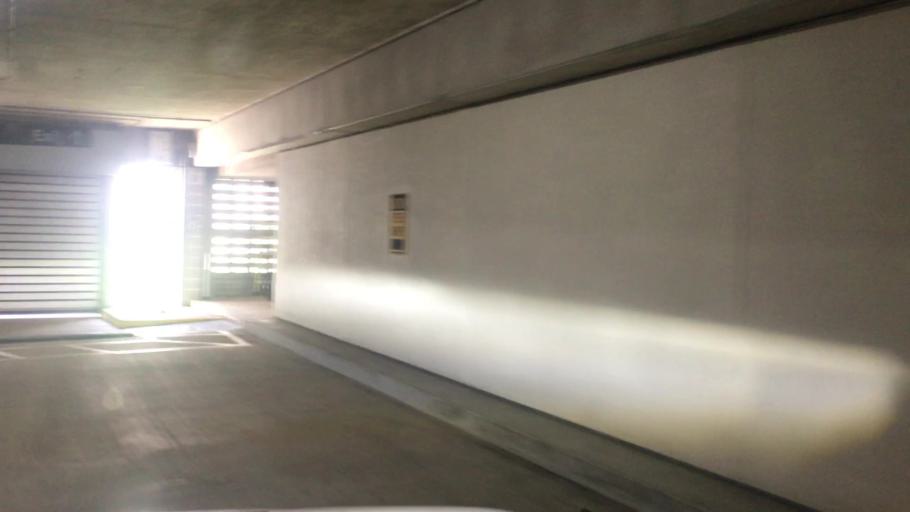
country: US
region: Texas
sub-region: Harris County
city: Bunker Hill Village
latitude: 29.7425
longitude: -95.5597
